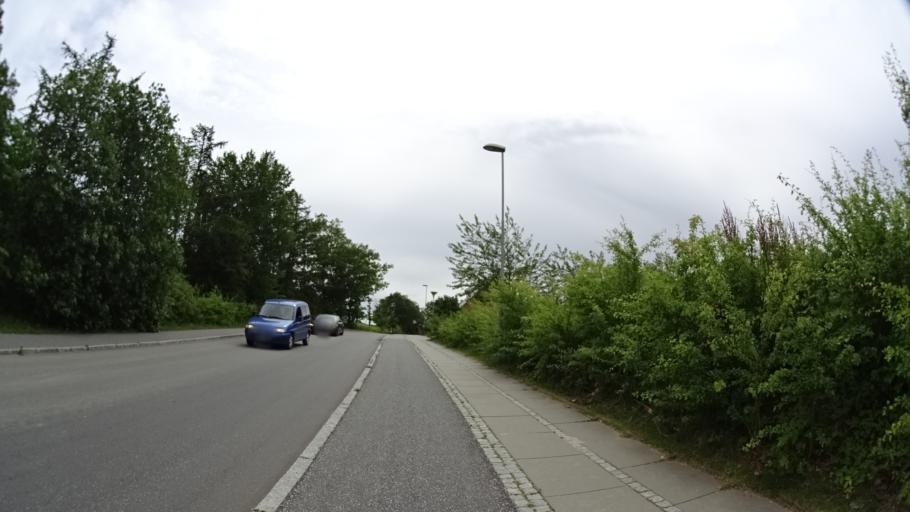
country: DK
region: Central Jutland
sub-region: Arhus Kommune
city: Stavtrup
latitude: 56.1216
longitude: 10.1333
